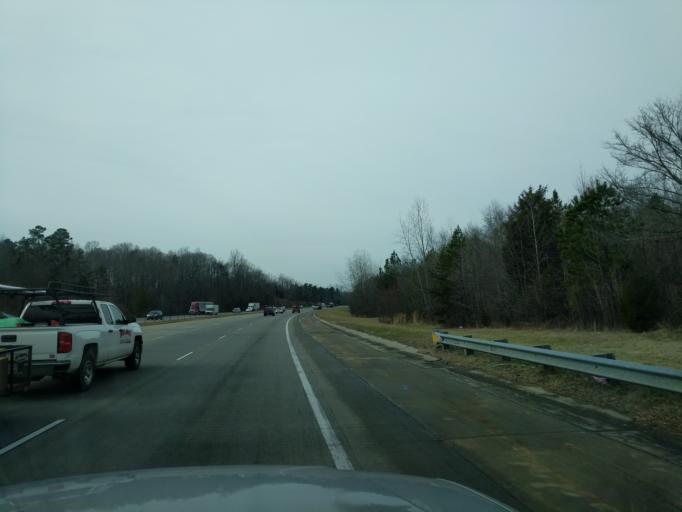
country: US
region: North Carolina
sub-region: Mecklenburg County
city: Huntersville
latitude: 35.3411
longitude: -80.8857
